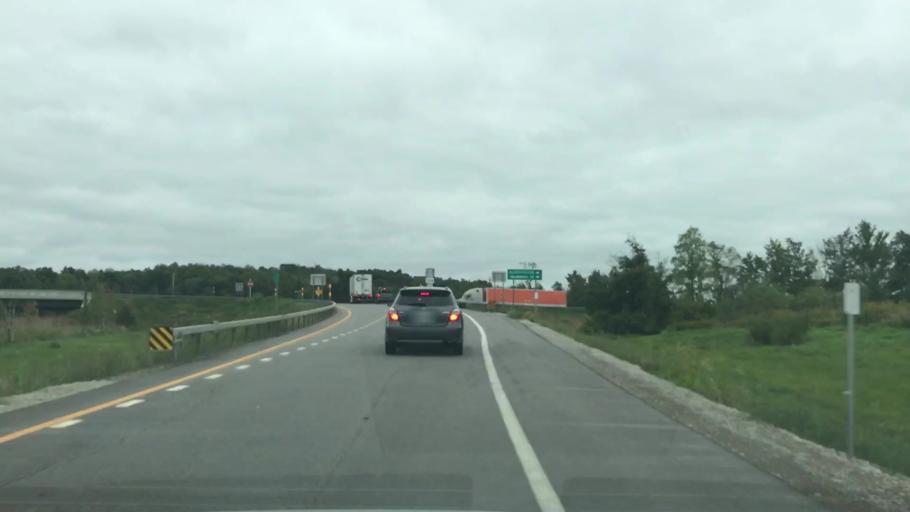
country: US
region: New York
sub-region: Erie County
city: Springville
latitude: 42.4618
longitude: -78.6962
